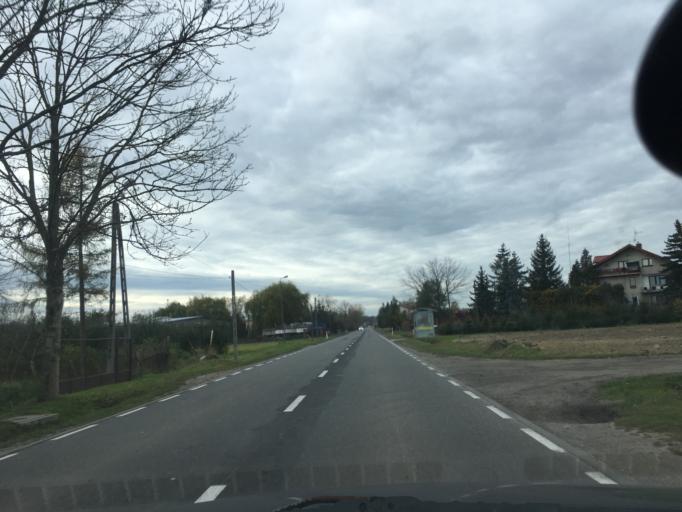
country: PL
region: Masovian Voivodeship
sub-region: Powiat piaseczynski
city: Tarczyn
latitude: 51.9787
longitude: 20.8493
